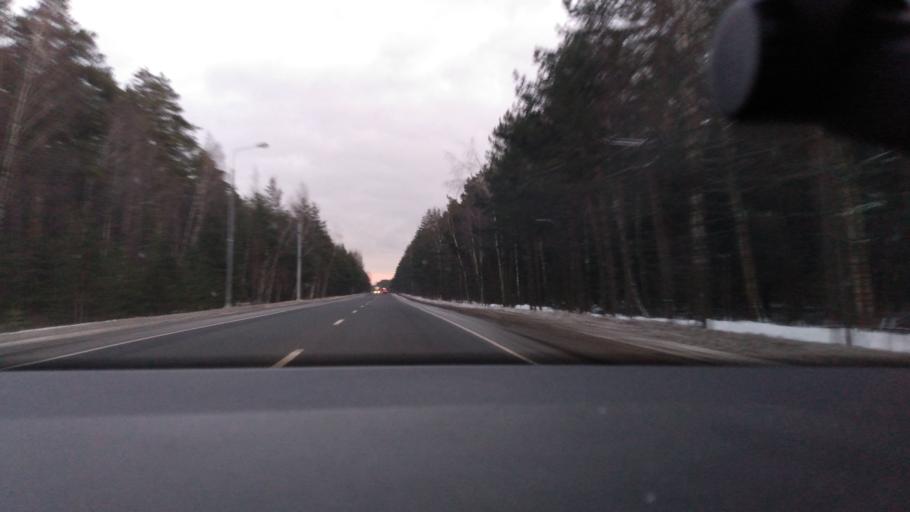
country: RU
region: Moskovskaya
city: Il'inskiy Pogost
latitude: 55.4828
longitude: 38.9295
